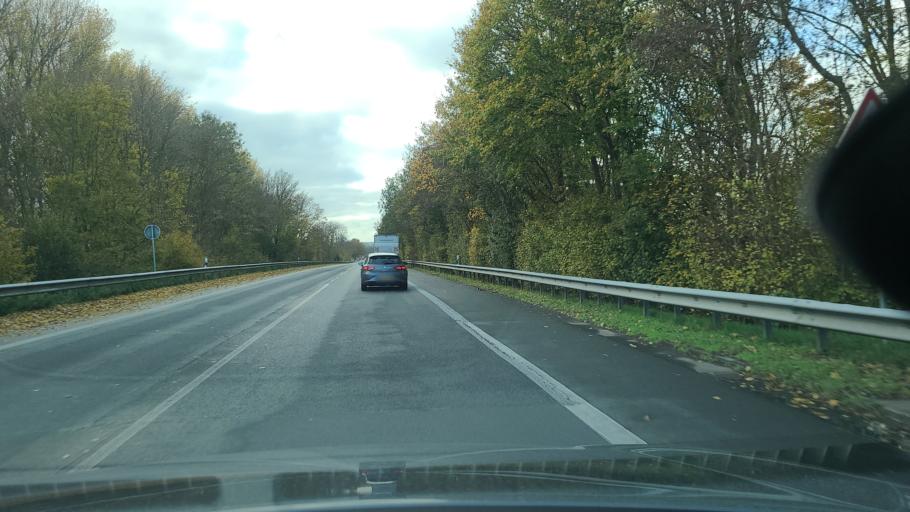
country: DE
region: North Rhine-Westphalia
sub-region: Regierungsbezirk Dusseldorf
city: Kranenburg
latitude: 51.8002
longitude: 6.0140
